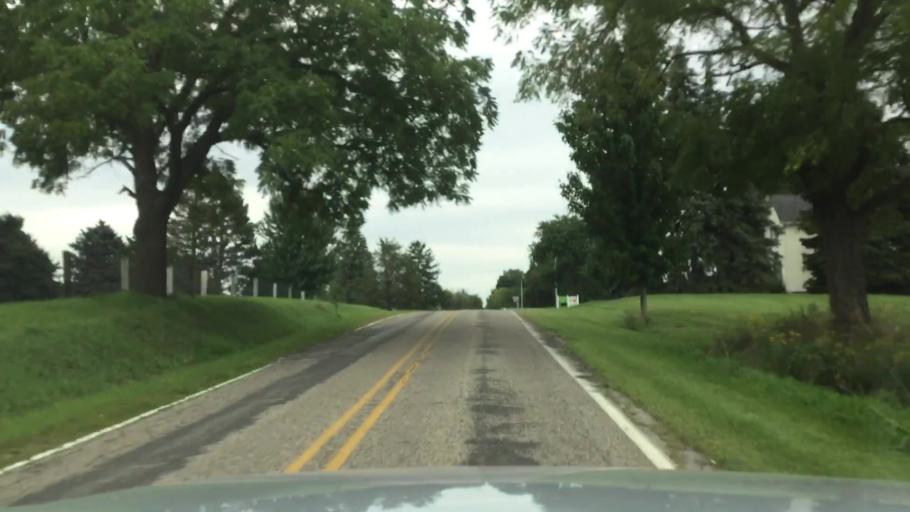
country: US
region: Michigan
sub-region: Shiawassee County
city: Durand
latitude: 42.8946
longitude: -84.0691
